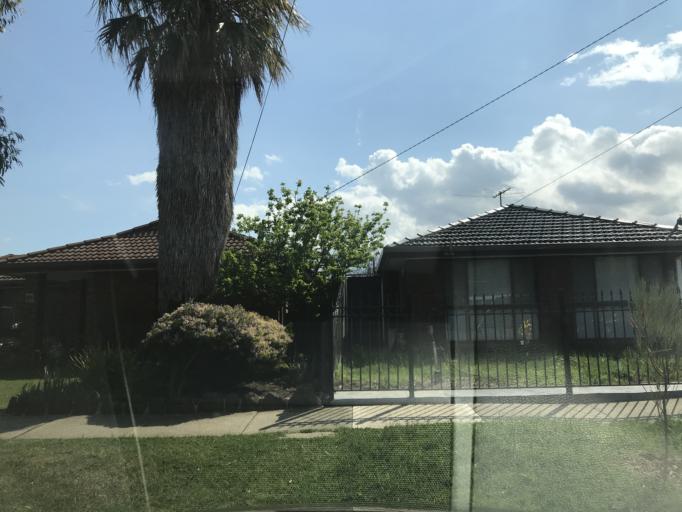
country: AU
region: Victoria
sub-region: Wyndham
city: Hoppers Crossing
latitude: -37.8715
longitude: 144.7099
